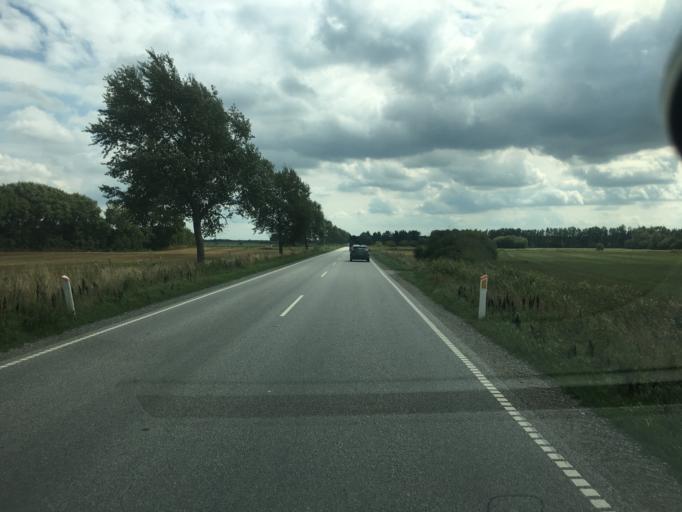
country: DK
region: South Denmark
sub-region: Aabenraa Kommune
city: Tinglev
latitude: 54.9787
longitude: 9.2972
